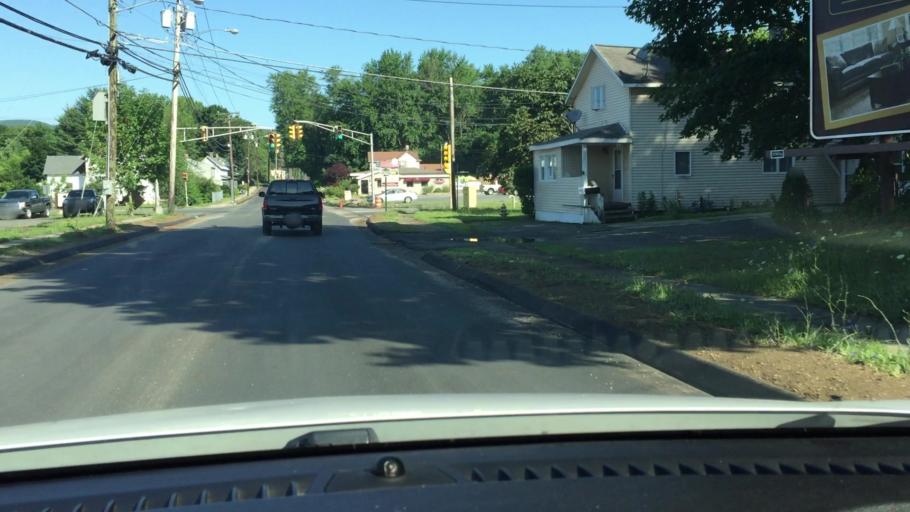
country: US
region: Massachusetts
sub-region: Berkshire County
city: Pittsfield
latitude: 42.4754
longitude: -73.2642
